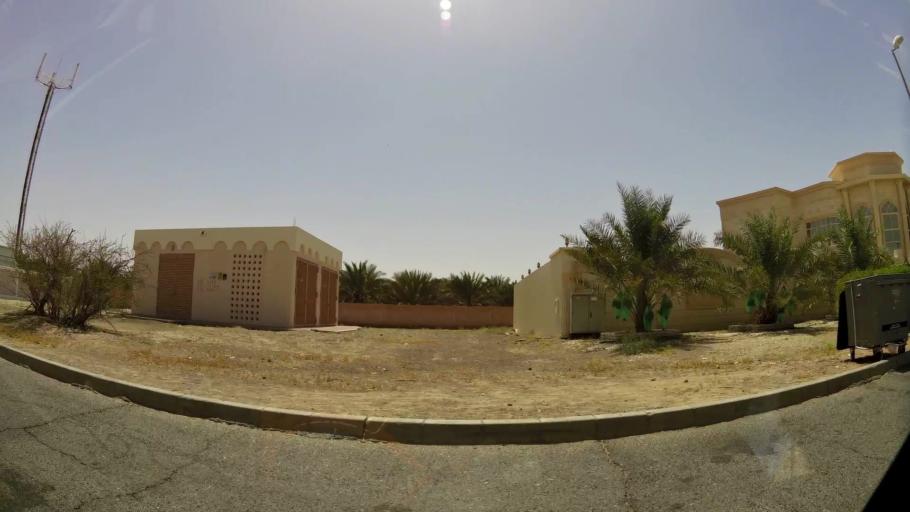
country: OM
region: Al Buraimi
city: Al Buraymi
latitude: 24.2771
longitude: 55.7758
